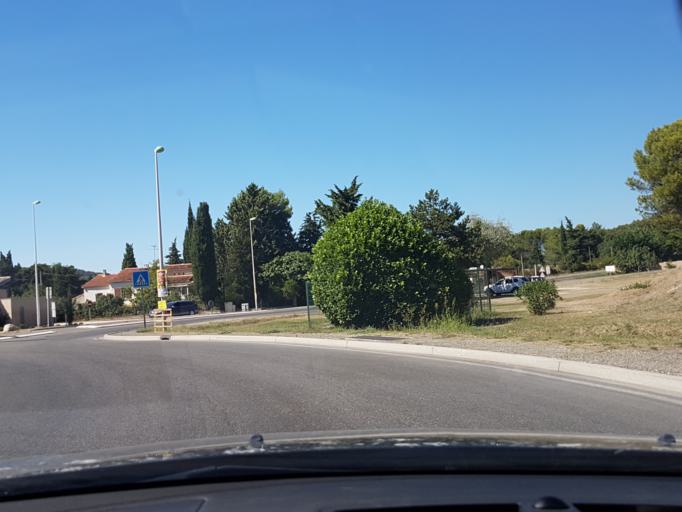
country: FR
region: Provence-Alpes-Cote d'Azur
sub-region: Departement des Bouches-du-Rhone
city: Orgon
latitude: 43.7928
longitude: 5.0294
